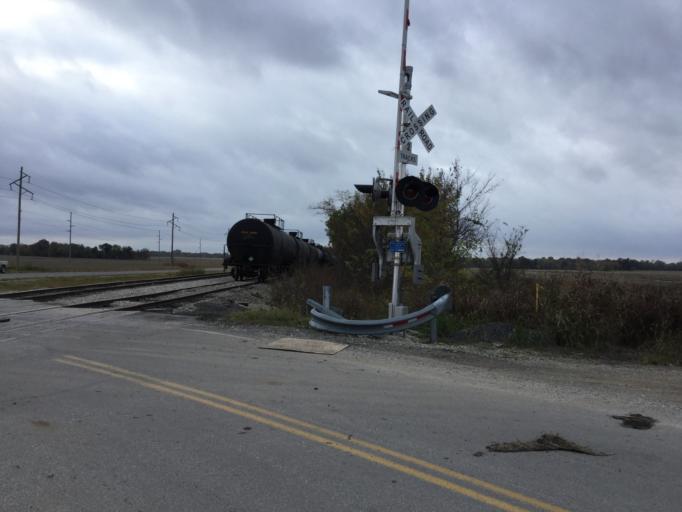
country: US
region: Kansas
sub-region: Montgomery County
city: Coffeyville
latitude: 37.0796
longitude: -95.6022
